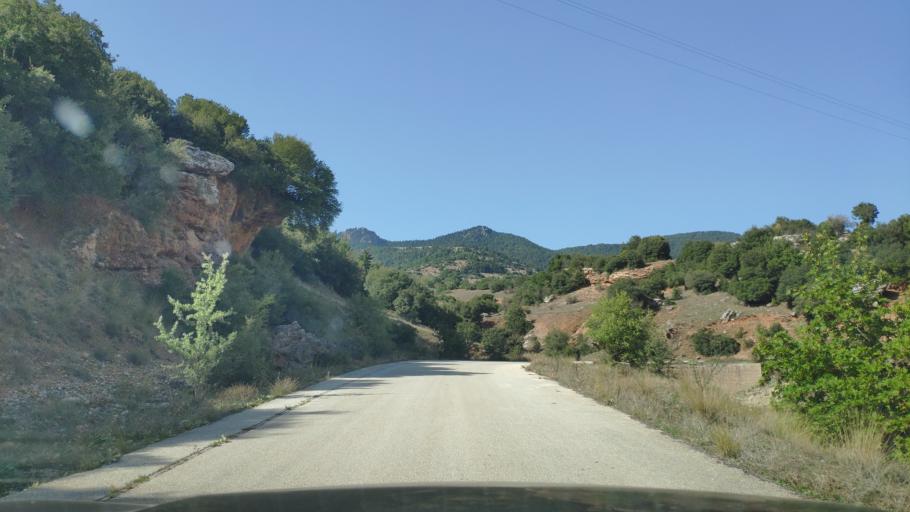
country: GR
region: West Greece
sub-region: Nomos Achaias
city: Aiyira
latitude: 37.9864
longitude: 22.3578
